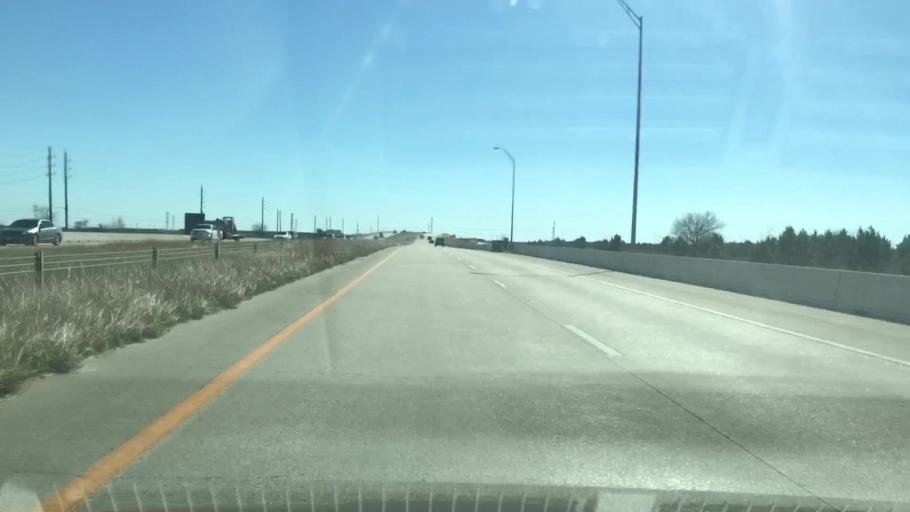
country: US
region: Texas
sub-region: Harris County
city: Cypress
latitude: 29.9277
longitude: -95.7629
